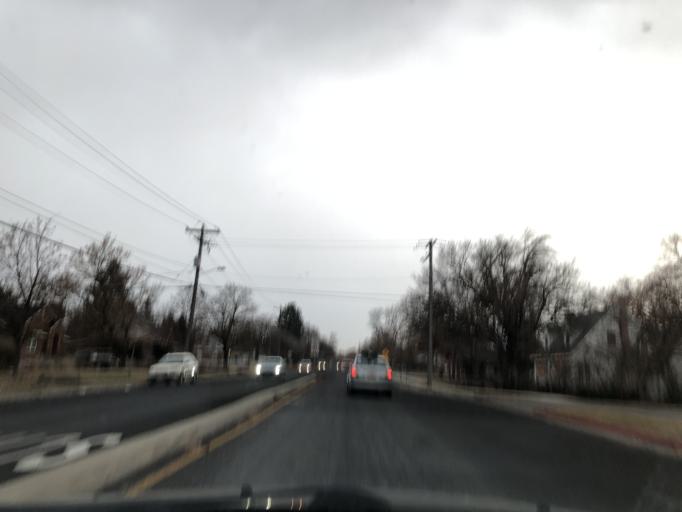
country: US
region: Utah
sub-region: Cache County
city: Logan
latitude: 41.7477
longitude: -111.8294
